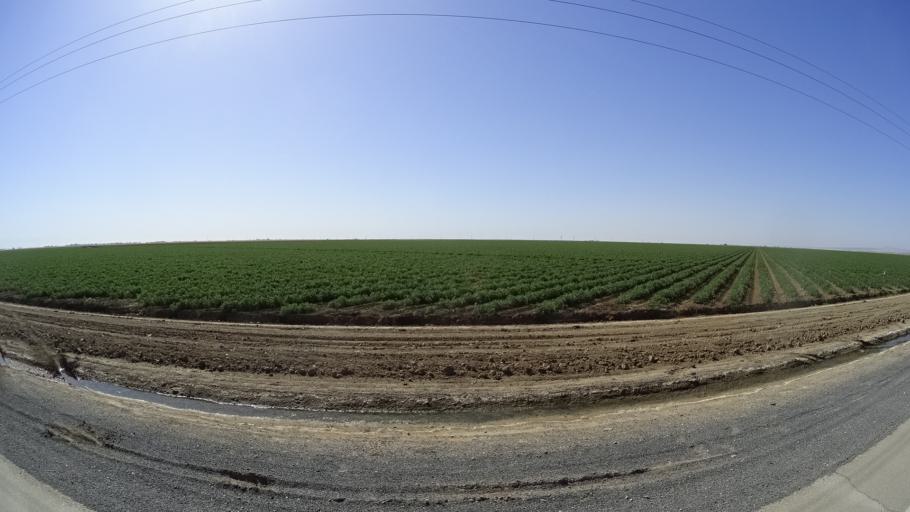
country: US
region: California
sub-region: Kings County
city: Lemoore Station
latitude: 36.2034
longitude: -119.9274
